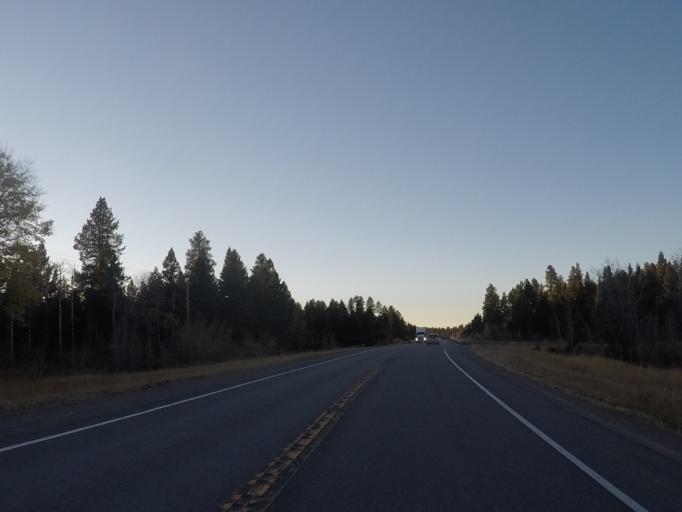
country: US
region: Montana
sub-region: Lewis and Clark County
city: Lincoln
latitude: 47.0095
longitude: -113.0597
